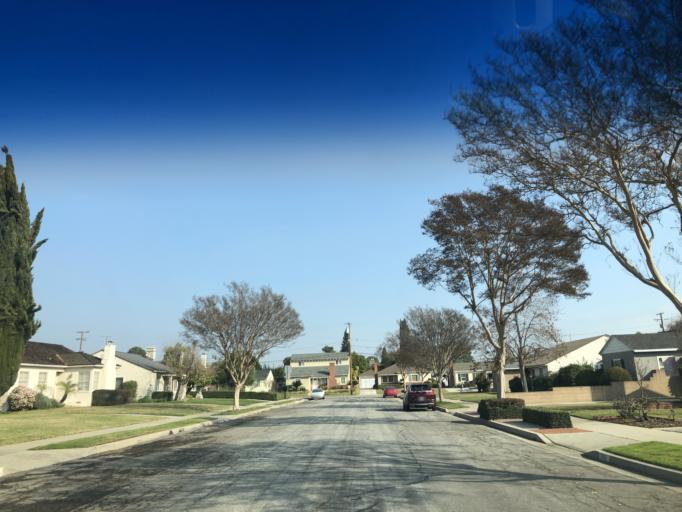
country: US
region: California
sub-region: Los Angeles County
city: East San Gabriel
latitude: 34.1072
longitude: -118.0874
